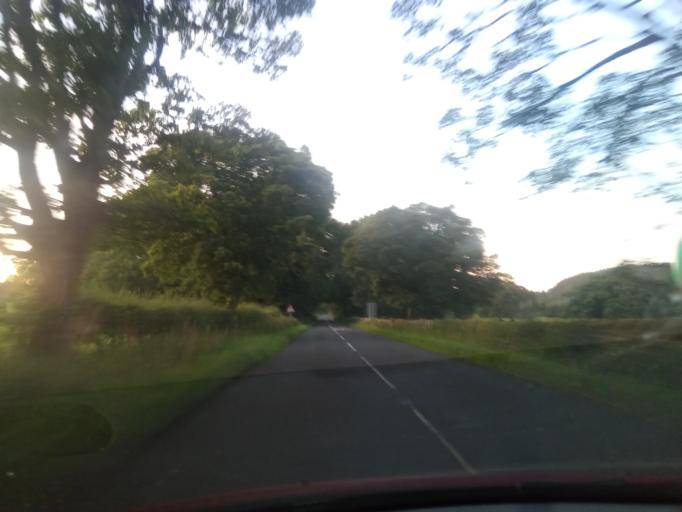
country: GB
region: England
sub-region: Northumberland
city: Bardon Mill
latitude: 54.8944
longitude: -2.3520
